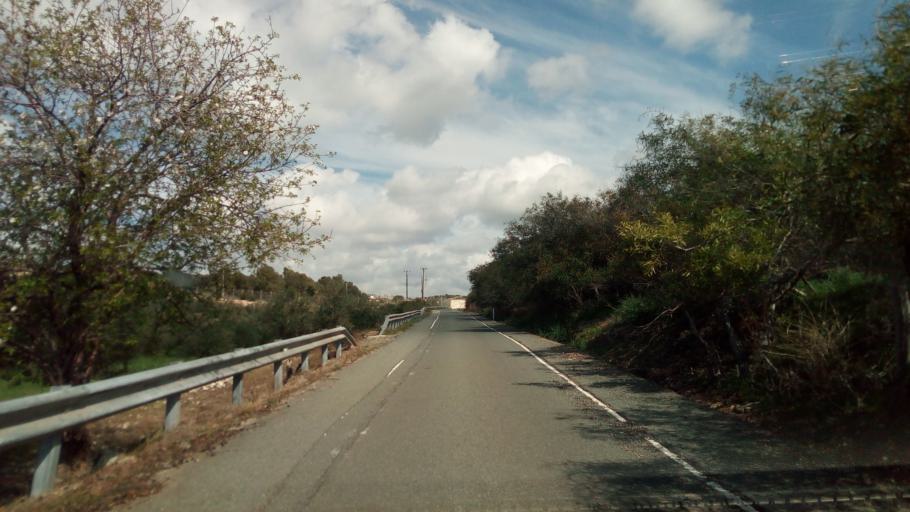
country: CY
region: Pafos
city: Mesogi
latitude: 34.7470
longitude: 32.5468
